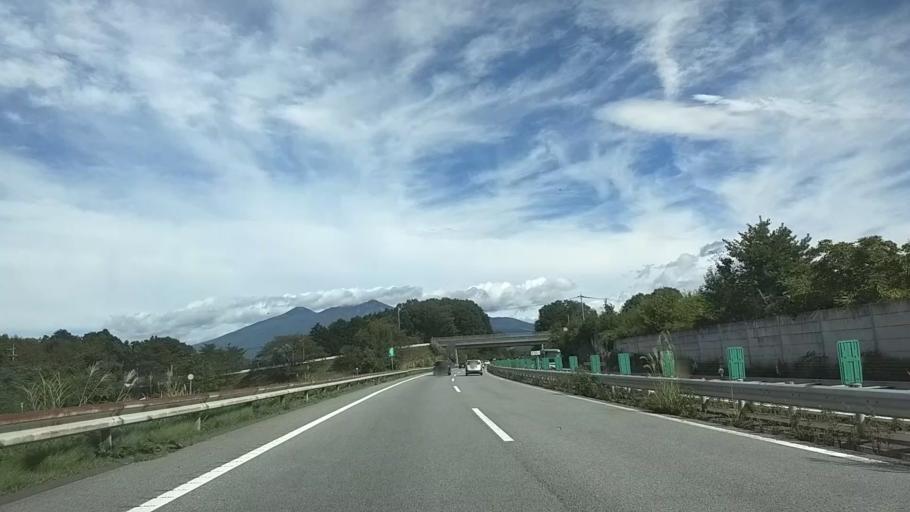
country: JP
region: Yamanashi
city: Nirasaki
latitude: 35.7983
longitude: 138.3953
